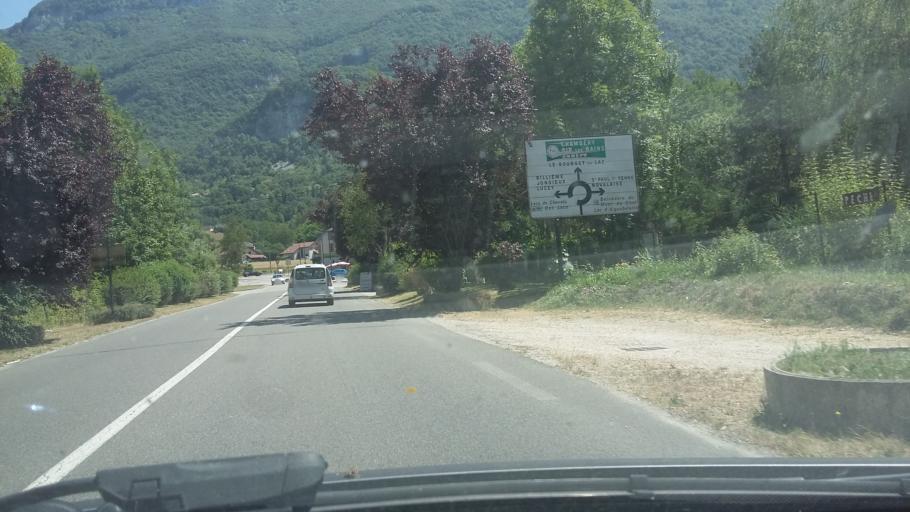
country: FR
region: Rhone-Alpes
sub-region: Departement de la Savoie
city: Yenne
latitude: 45.6913
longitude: 5.8132
